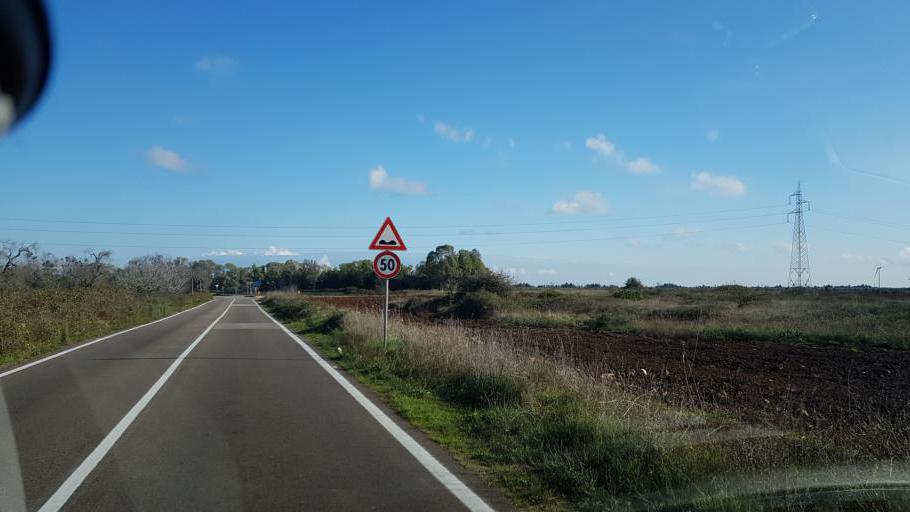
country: IT
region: Apulia
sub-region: Provincia di Lecce
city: Trepuzzi
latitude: 40.4473
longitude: 18.1051
